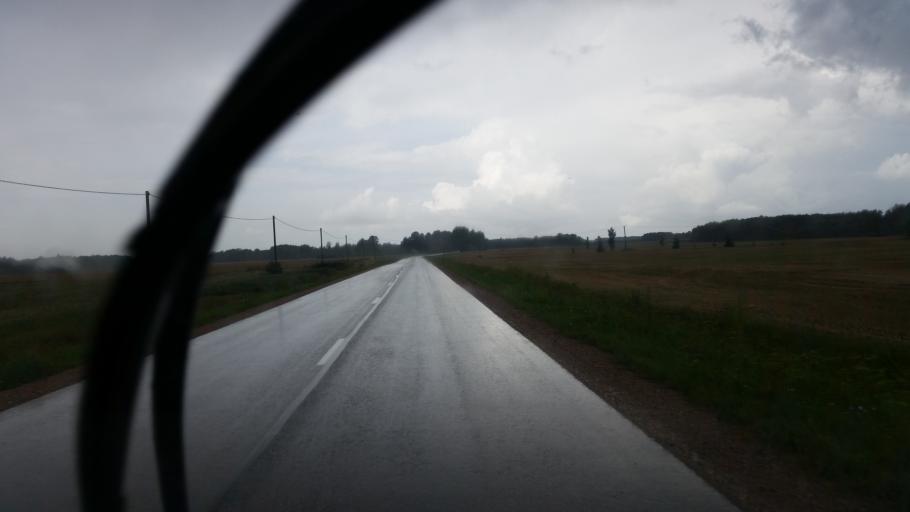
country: LV
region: Vecumnieki
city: Vecumnieki
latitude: 56.4316
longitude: 24.4068
